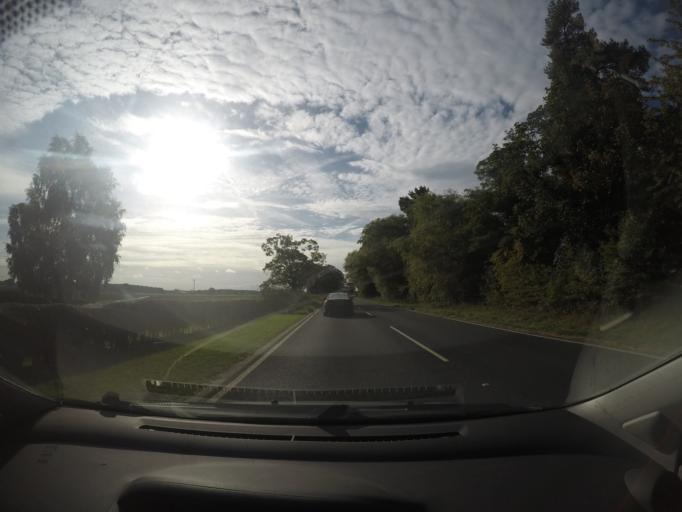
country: GB
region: England
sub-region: City of York
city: Deighton
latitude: 53.9037
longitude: -1.0493
